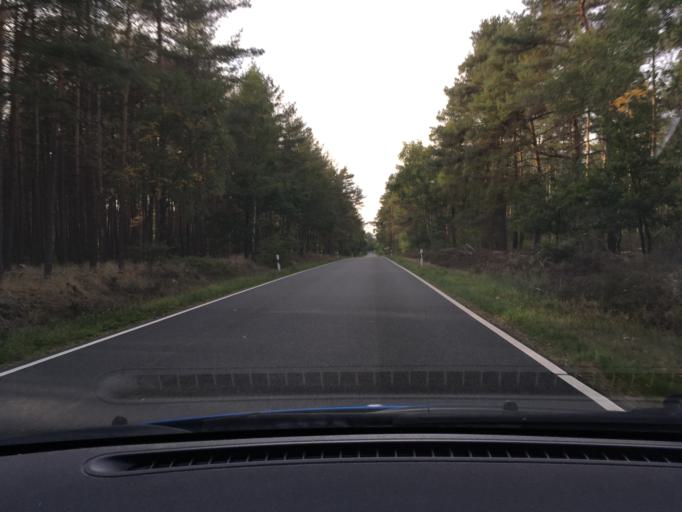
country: DE
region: Lower Saxony
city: Fassberg
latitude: 52.9039
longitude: 10.1014
